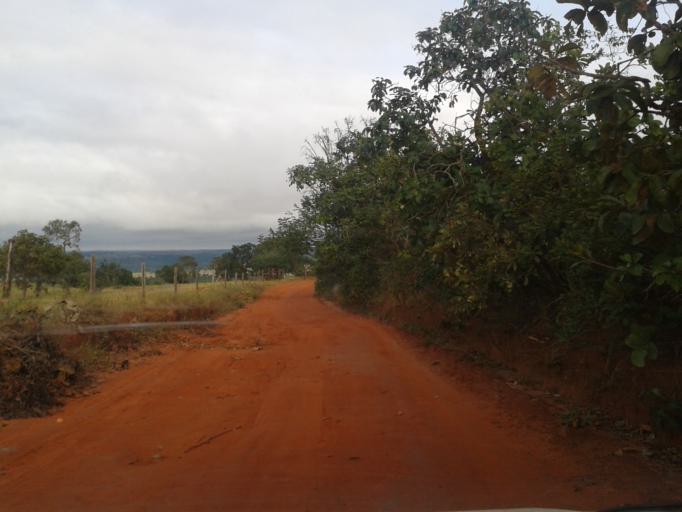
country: BR
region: Minas Gerais
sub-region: Campina Verde
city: Campina Verde
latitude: -19.4029
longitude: -49.6273
